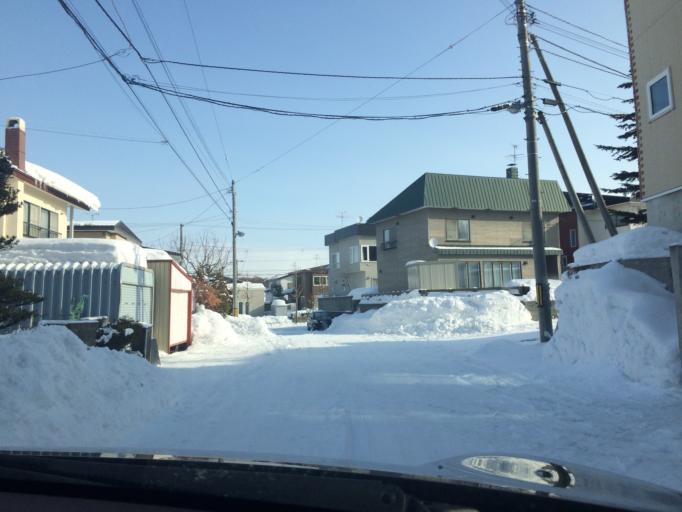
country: JP
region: Hokkaido
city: Ebetsu
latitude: 43.0419
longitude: 141.4922
